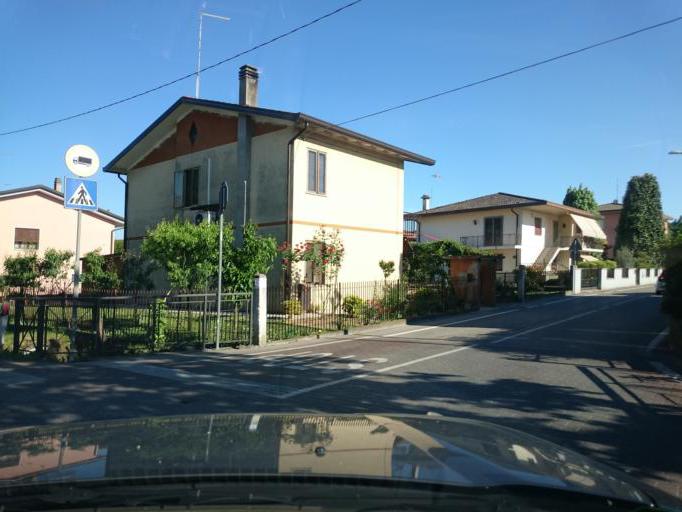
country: IT
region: Veneto
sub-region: Provincia di Venezia
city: Noale
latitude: 45.5479
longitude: 12.0673
